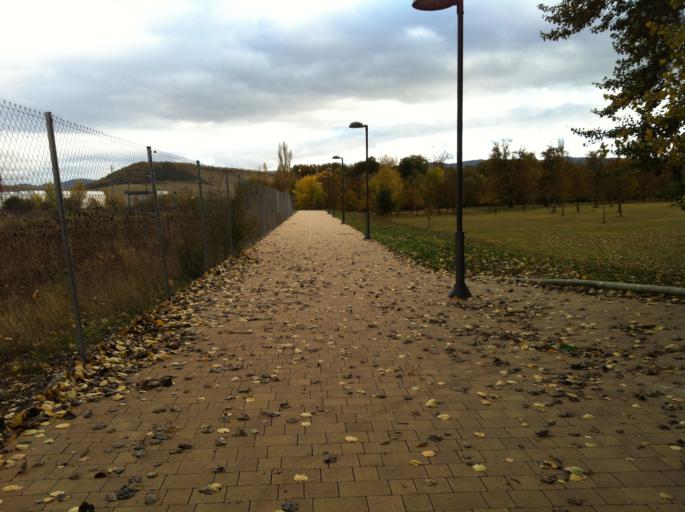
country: ES
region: Basque Country
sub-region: Provincia de Alava
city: Gasteiz / Vitoria
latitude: 42.8304
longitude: -2.6597
